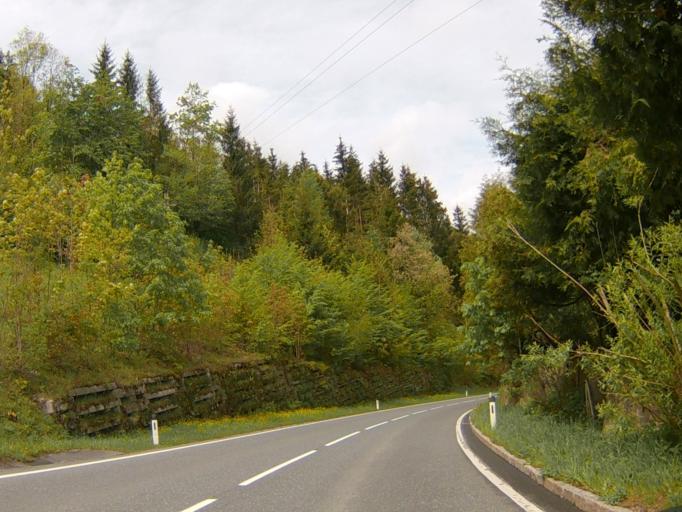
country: AT
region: Salzburg
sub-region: Politischer Bezirk Hallein
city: Hallein
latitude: 47.6722
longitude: 13.0850
